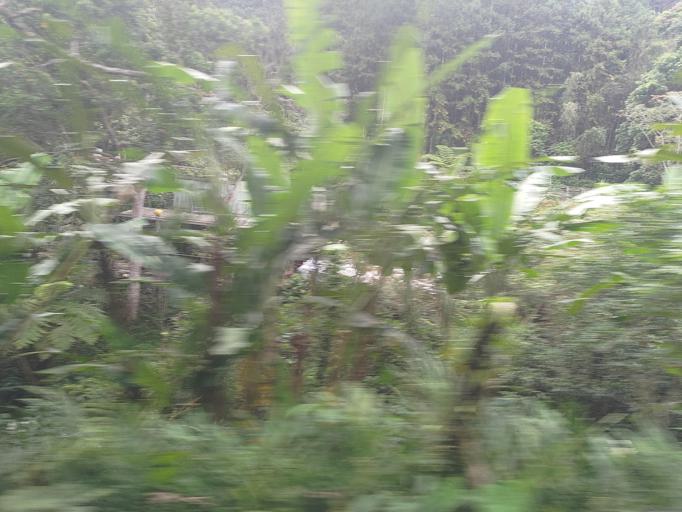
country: TW
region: Taiwan
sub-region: Hsinchu
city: Hsinchu
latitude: 24.6139
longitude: 121.0420
